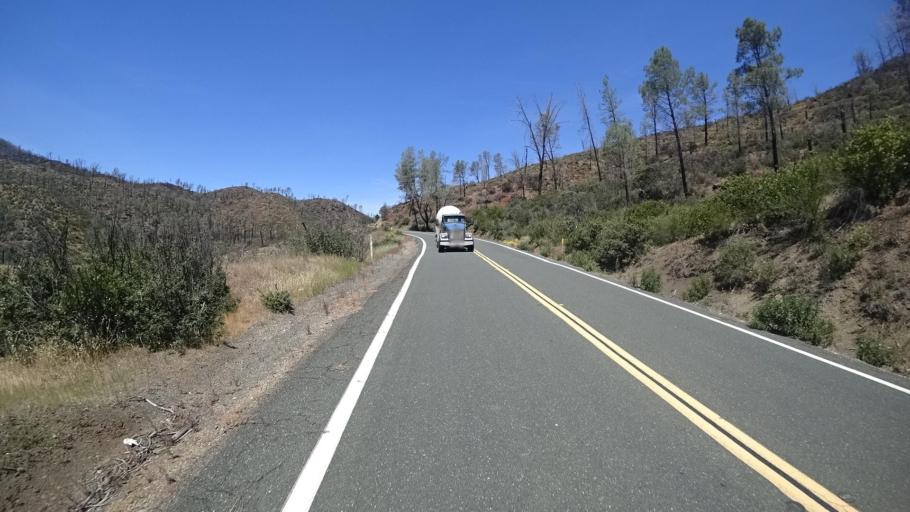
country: US
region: California
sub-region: Lake County
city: Hidden Valley Lake
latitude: 38.7120
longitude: -122.4790
